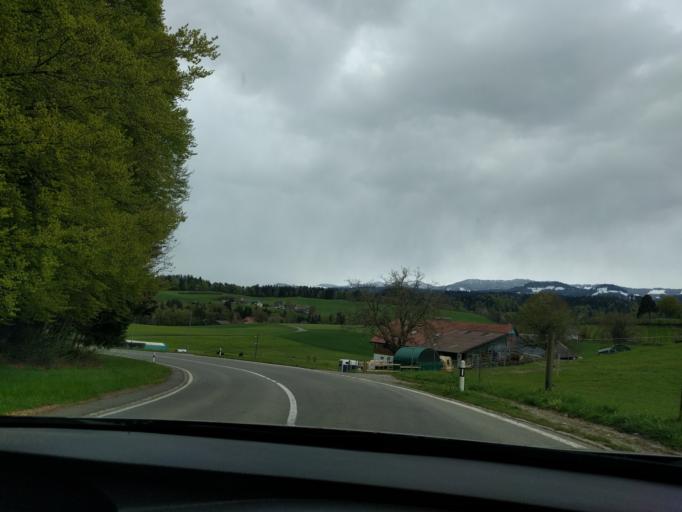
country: CH
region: Fribourg
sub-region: Sense District
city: Heitenried
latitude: 46.8219
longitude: 7.3025
